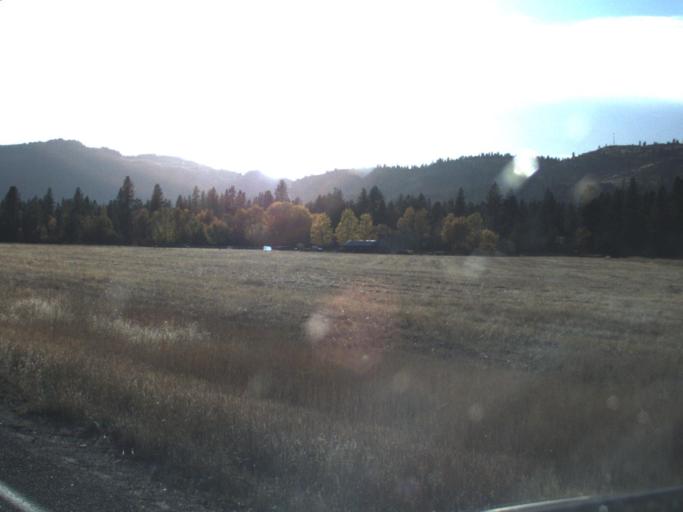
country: CA
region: British Columbia
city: Rossland
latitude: 48.8371
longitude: -117.9048
